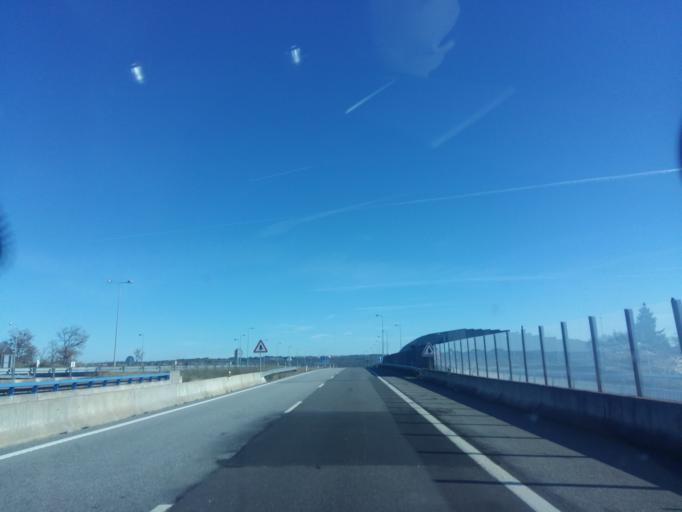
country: PT
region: Guarda
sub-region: Guarda
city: Sequeira
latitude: 40.6048
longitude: -7.0677
